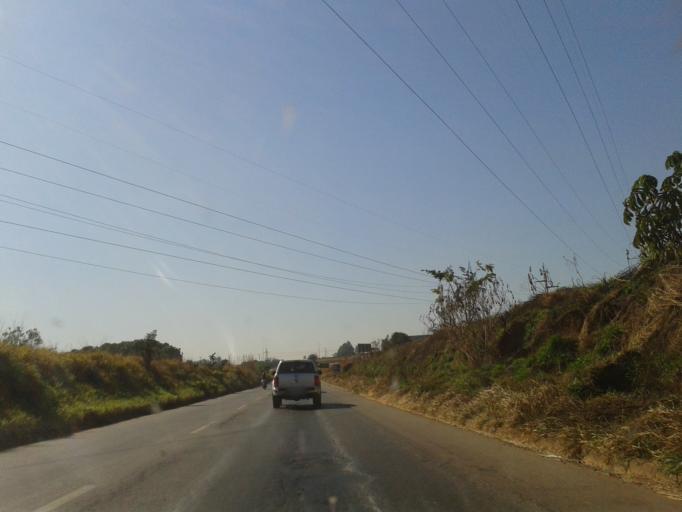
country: BR
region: Goias
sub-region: Aparecida De Goiania
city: Aparecida de Goiania
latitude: -16.7872
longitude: -49.2434
